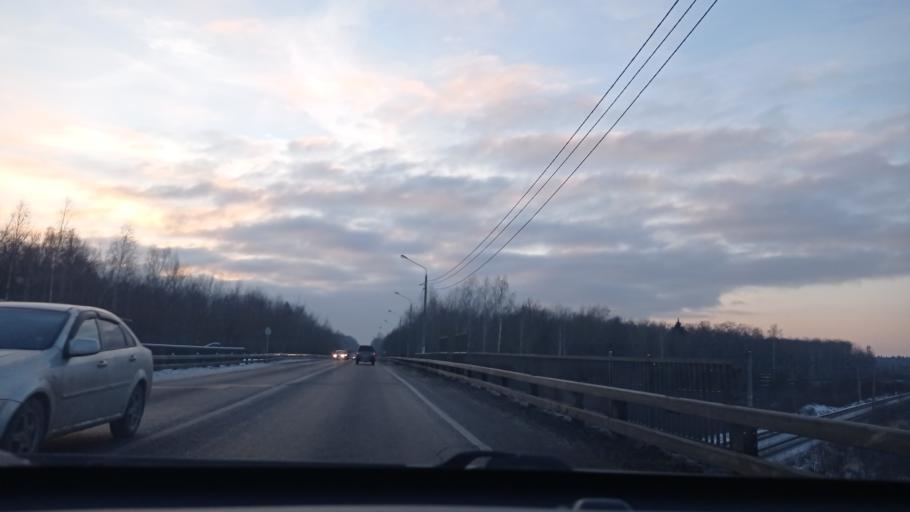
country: RU
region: Moskovskaya
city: Troitsk
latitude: 55.2730
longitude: 37.1320
